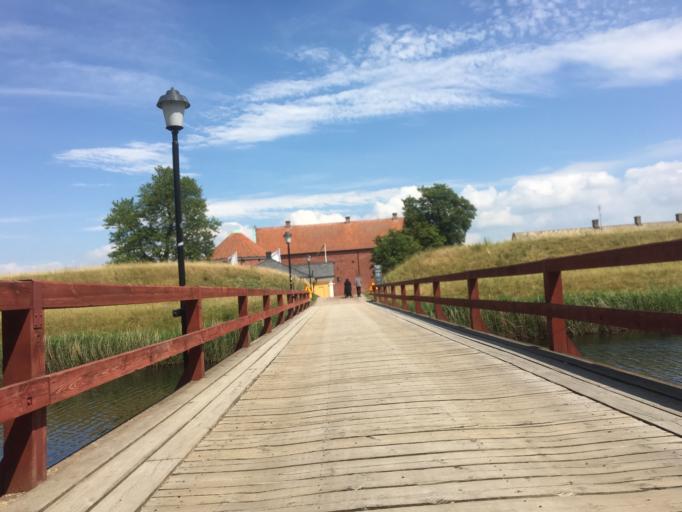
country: SE
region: Skane
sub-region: Landskrona
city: Landskrona
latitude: 55.8722
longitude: 12.8205
